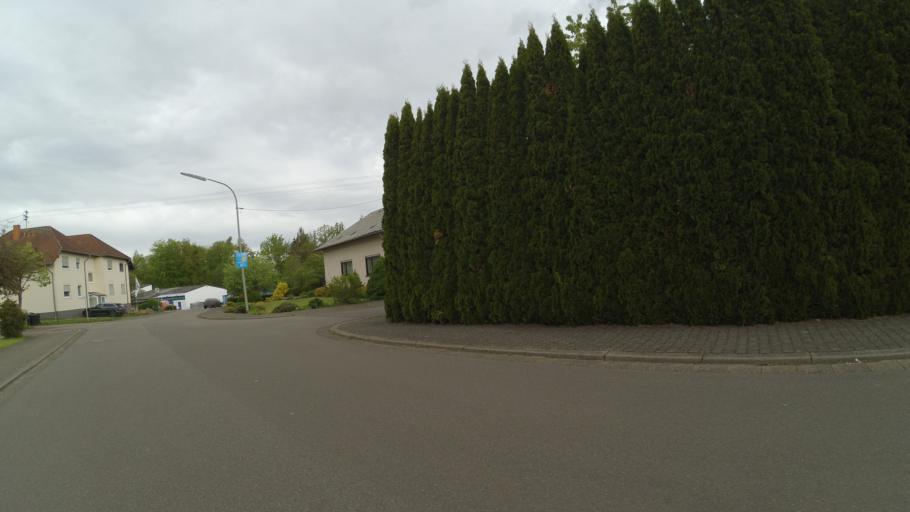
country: DE
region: Saarland
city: Orscholz
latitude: 49.5109
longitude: 6.5290
